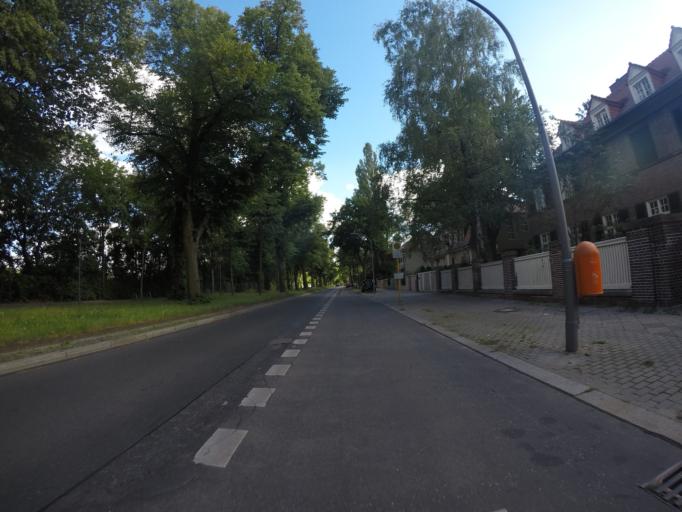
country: DE
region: Berlin
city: Dahlem
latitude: 52.4617
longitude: 13.2874
